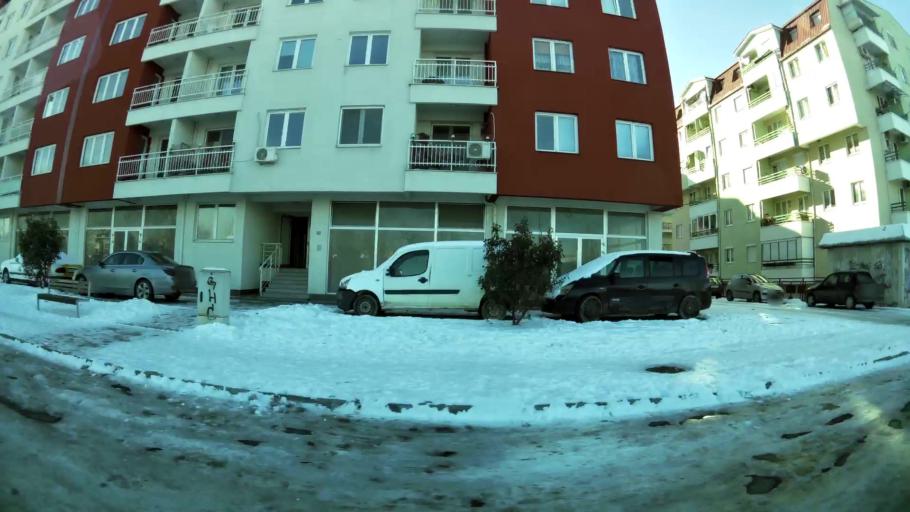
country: MK
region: Saraj
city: Saraj
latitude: 42.0050
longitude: 21.3419
